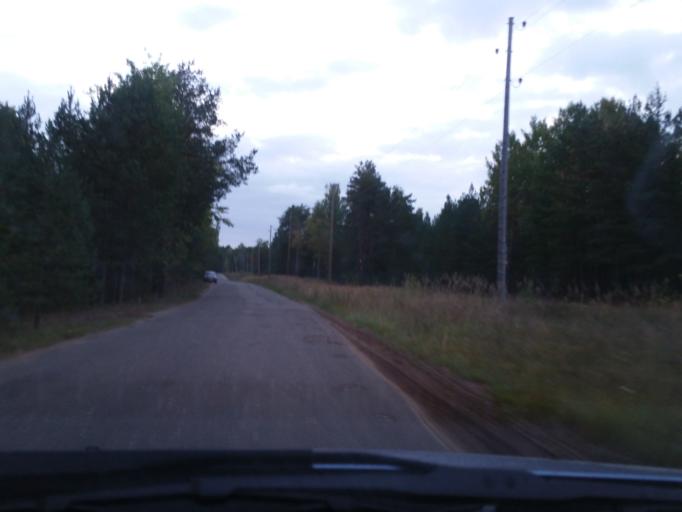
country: LV
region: Adazi
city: Adazi
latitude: 57.1177
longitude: 24.3630
